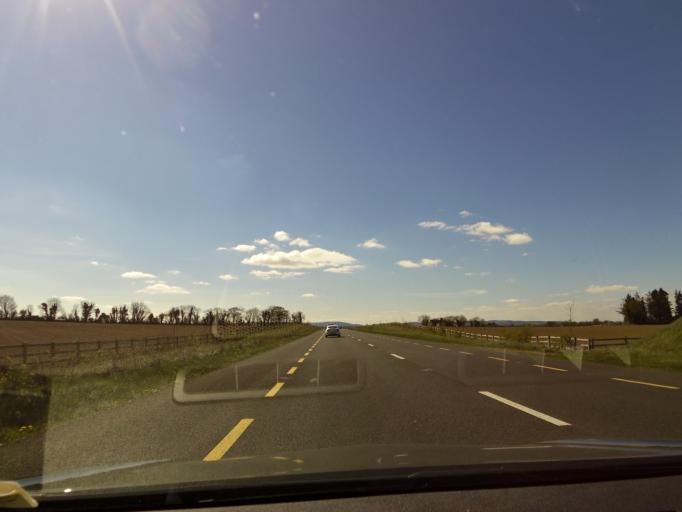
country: IE
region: Leinster
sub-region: Kildare
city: Athy
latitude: 52.9868
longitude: -6.9276
